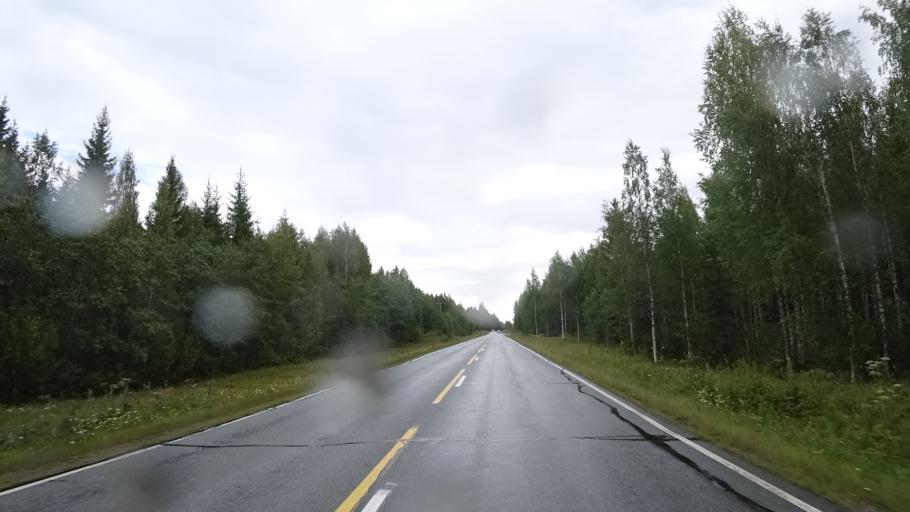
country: FI
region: North Karelia
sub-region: Keski-Karjala
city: Kesaelahti
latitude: 62.1073
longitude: 29.8072
